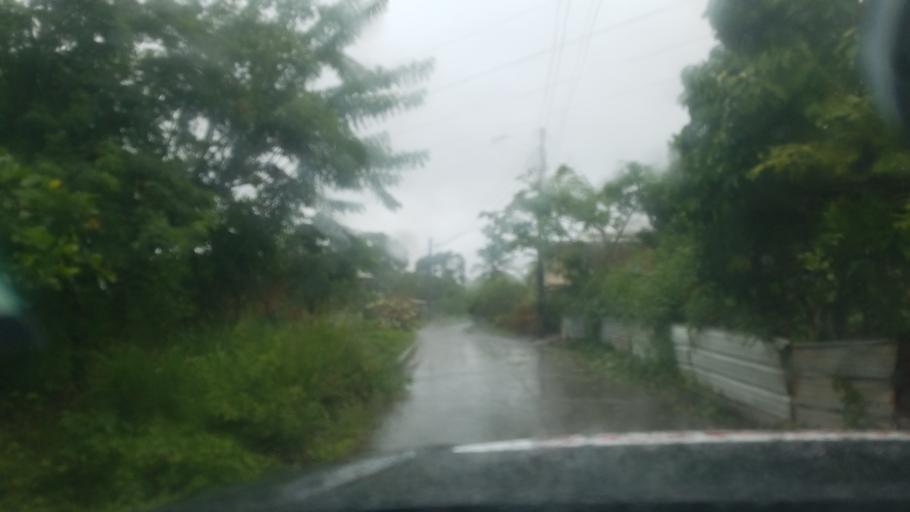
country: LC
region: Laborie Quarter
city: Laborie
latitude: 13.7581
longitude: -60.9777
